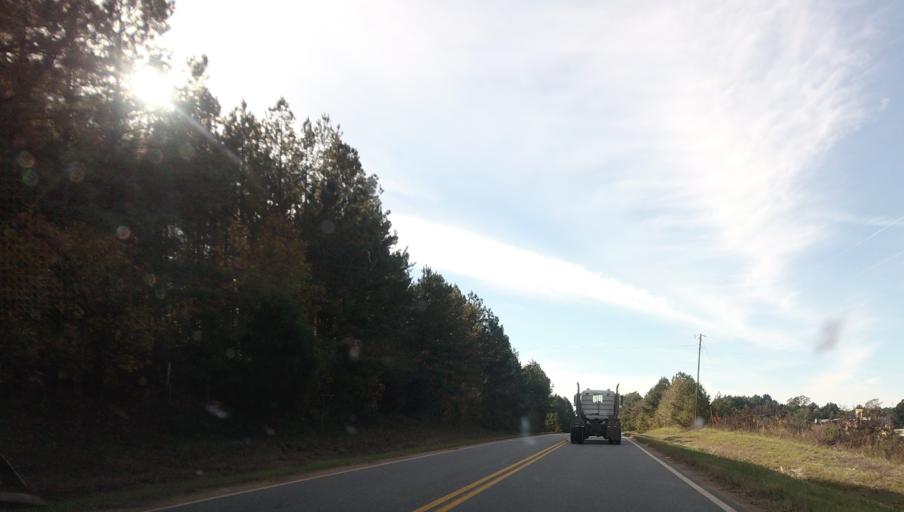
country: US
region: Georgia
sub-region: Talbot County
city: Talbotton
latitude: 32.7048
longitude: -84.4008
